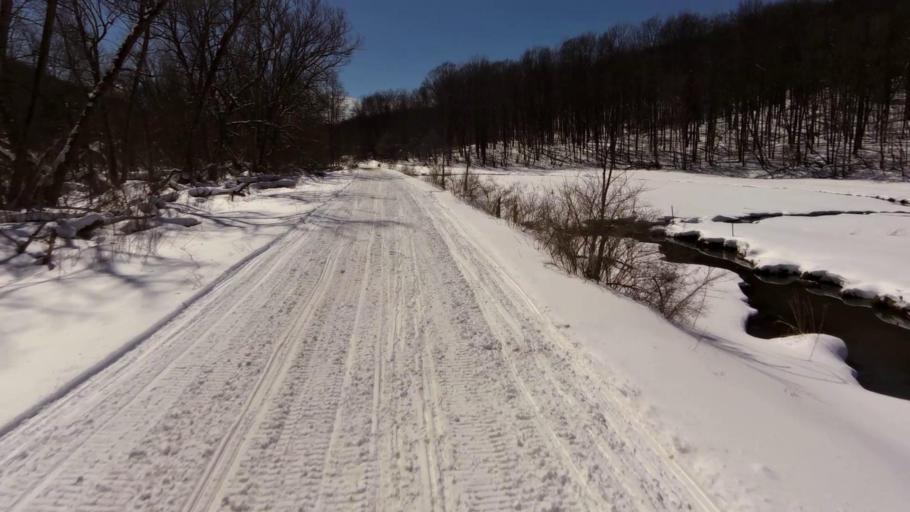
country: US
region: New York
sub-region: Cattaraugus County
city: Delevan
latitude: 42.4258
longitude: -78.4556
